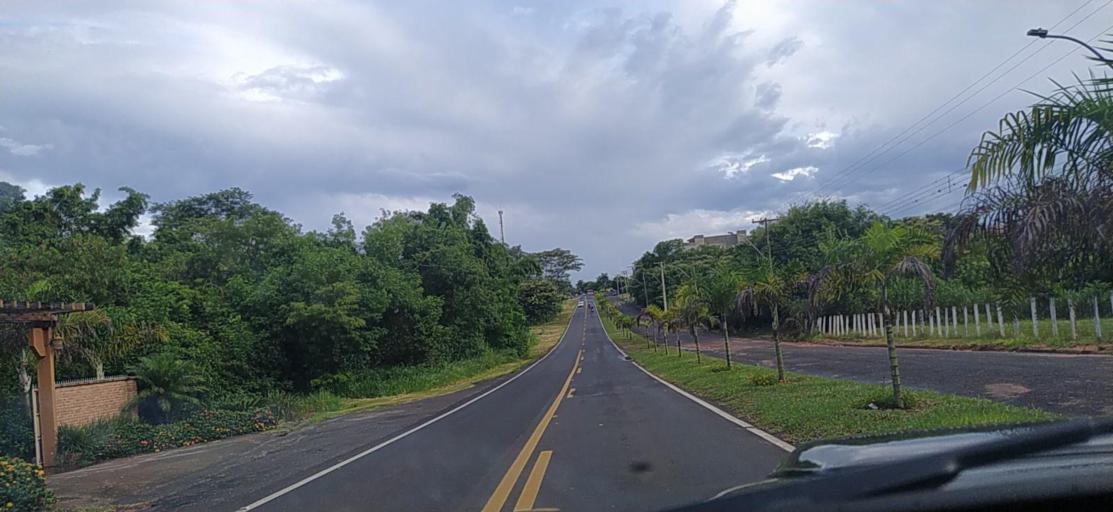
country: BR
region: Sao Paulo
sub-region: Pindorama
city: Pindorama
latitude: -21.1790
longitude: -48.9182
